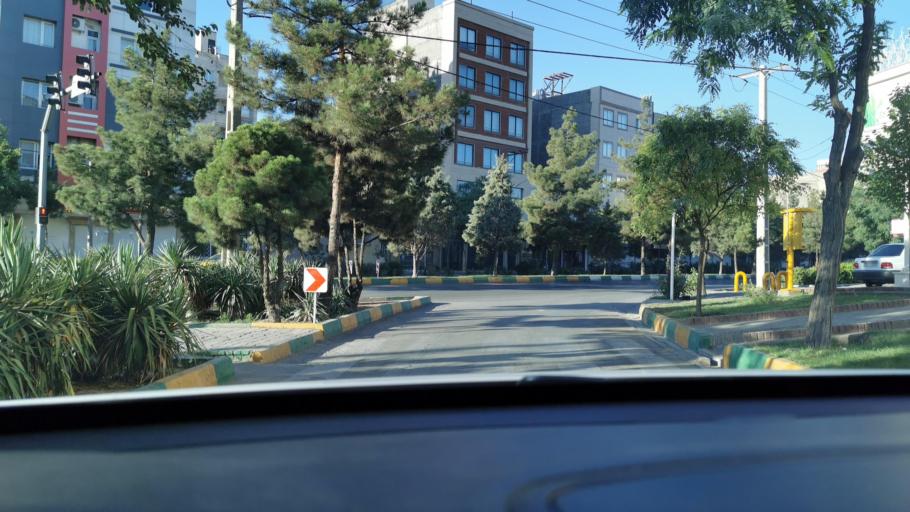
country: IR
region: Razavi Khorasan
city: Mashhad
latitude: 36.3587
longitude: 59.4913
